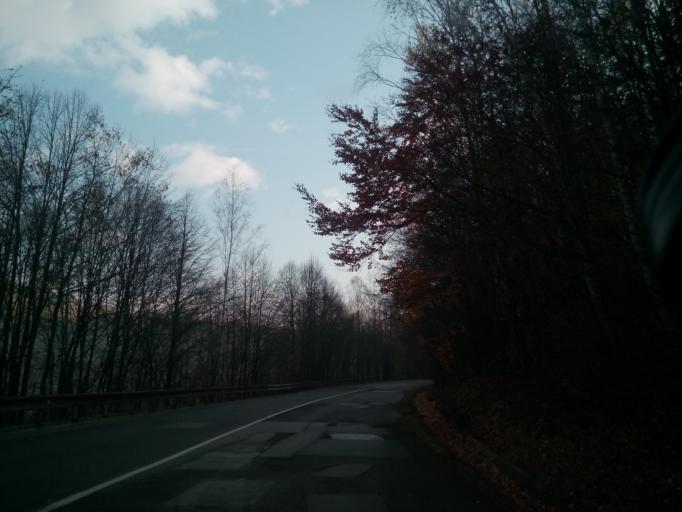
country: SK
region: Kosicky
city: Gelnica
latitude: 48.9053
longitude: 20.9818
